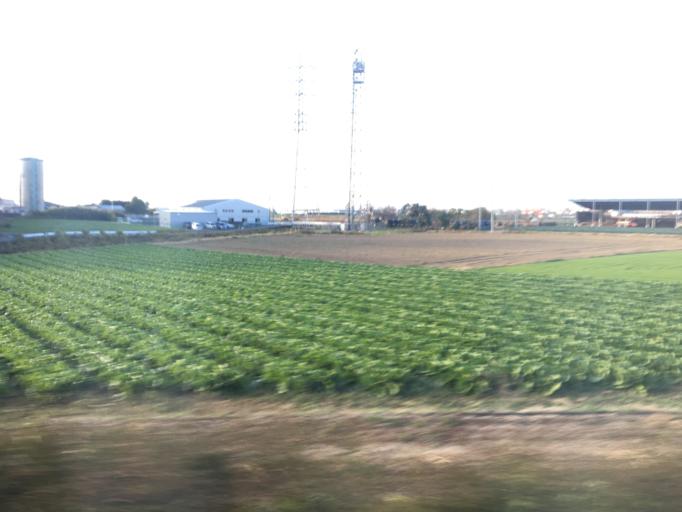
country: JP
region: Gunma
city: Isesaki
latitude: 36.3657
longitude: 139.2506
